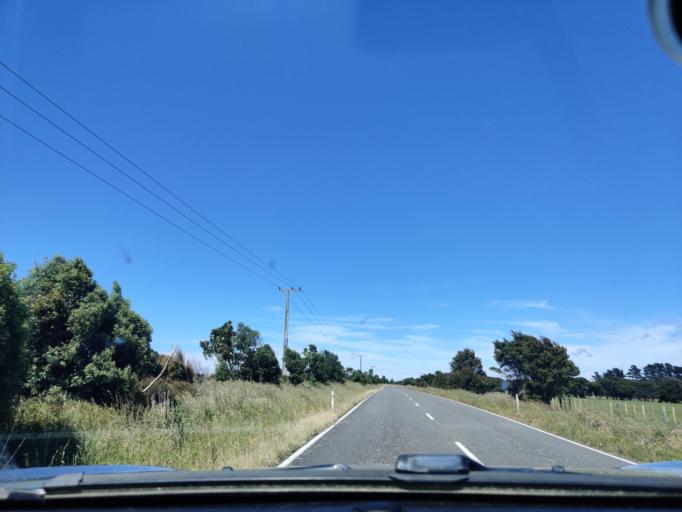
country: NZ
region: Wellington
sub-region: Upper Hutt City
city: Upper Hutt
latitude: -41.3252
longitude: 175.2450
